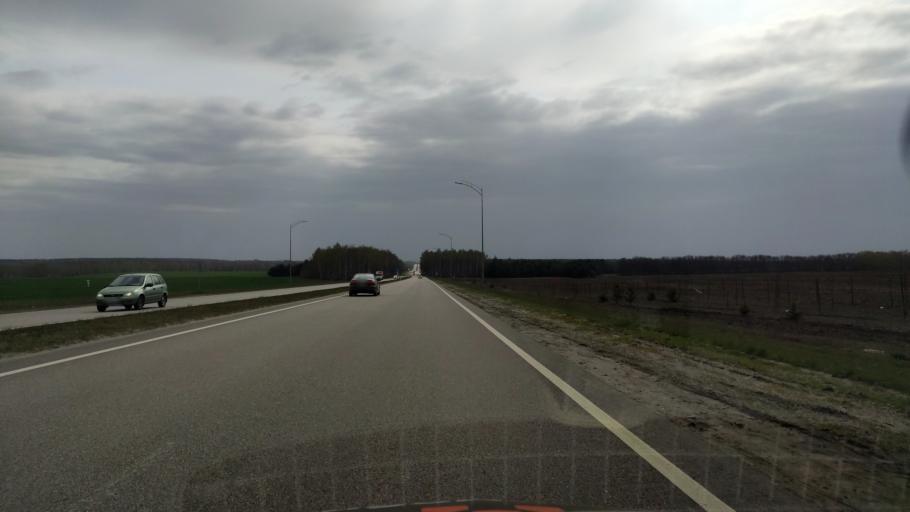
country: RU
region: Belgorod
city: Staryy Oskol
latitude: 51.4158
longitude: 37.8873
